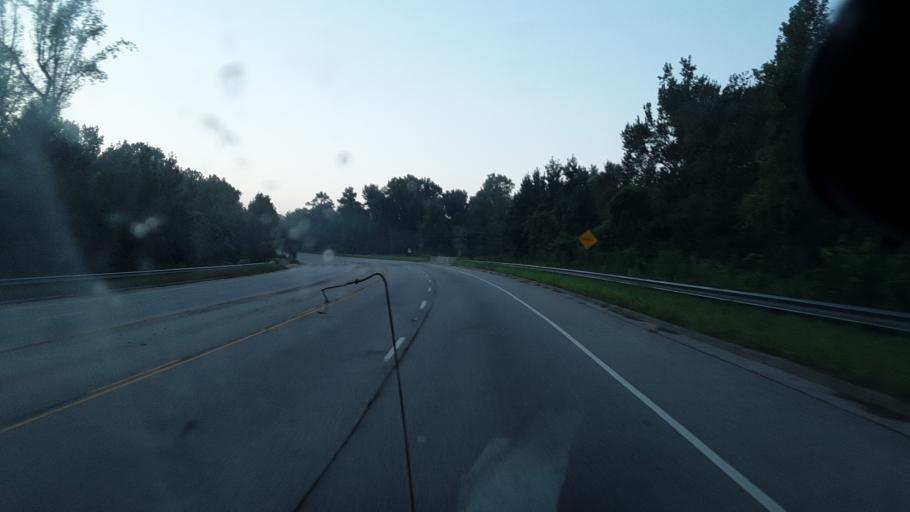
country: US
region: South Carolina
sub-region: Sumter County
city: South Sumter
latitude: 33.8757
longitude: -80.3353
